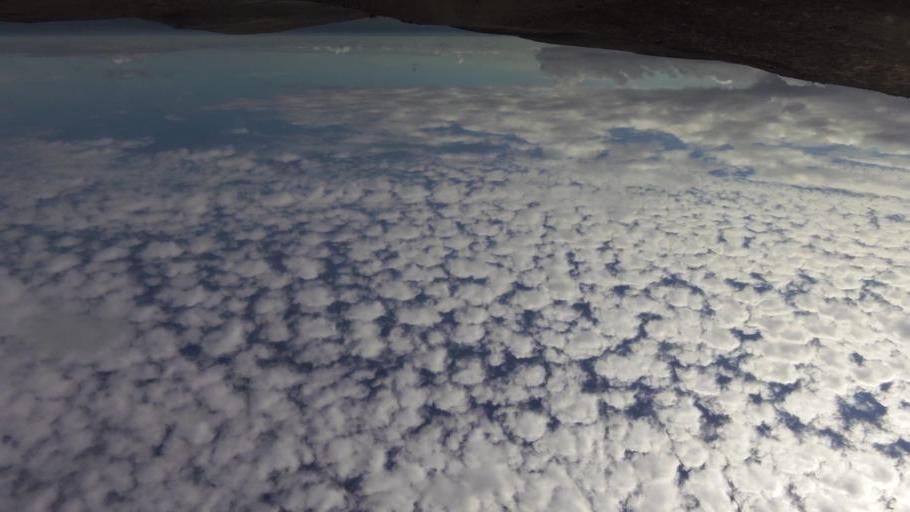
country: IS
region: West
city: Olafsvik
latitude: 65.6197
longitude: -24.2671
